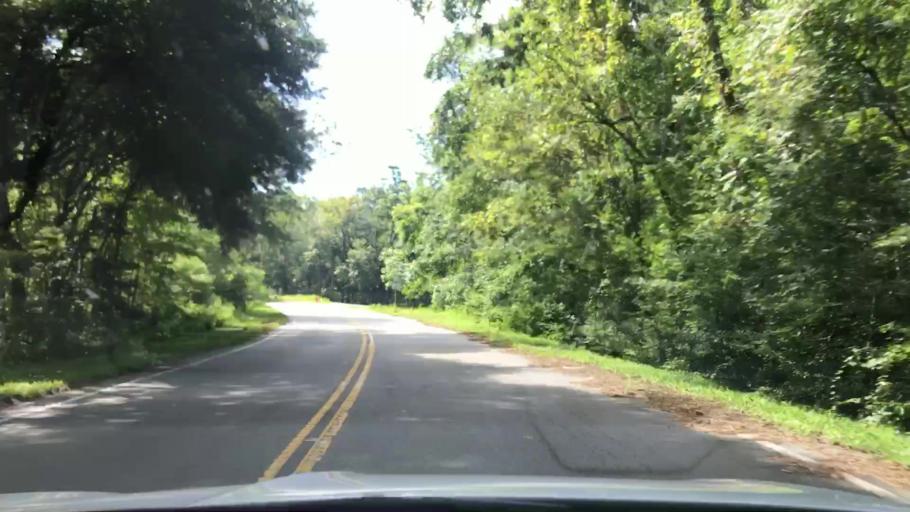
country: US
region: South Carolina
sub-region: Dorchester County
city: Centerville
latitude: 32.9479
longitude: -80.2026
